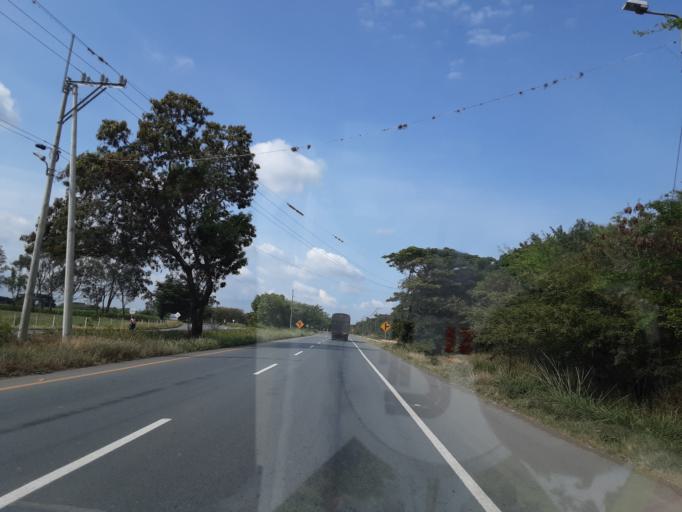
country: CO
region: Valle del Cauca
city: Guacari
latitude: 3.7739
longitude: -76.3265
